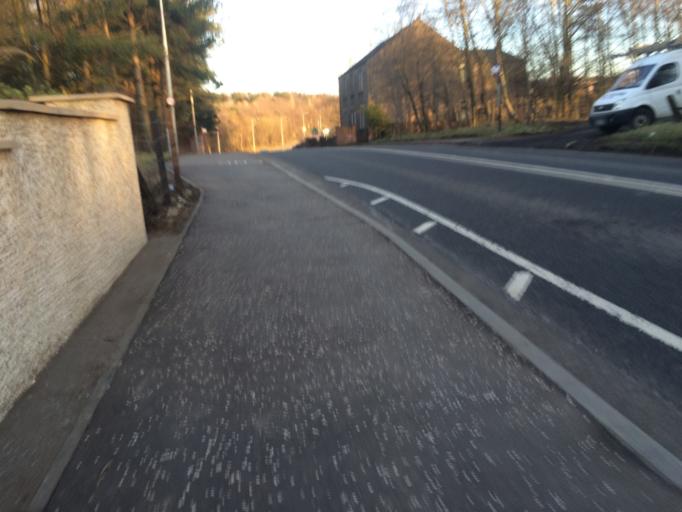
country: GB
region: Scotland
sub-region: Fife
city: Lochgelly
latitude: 56.1407
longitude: -3.3196
